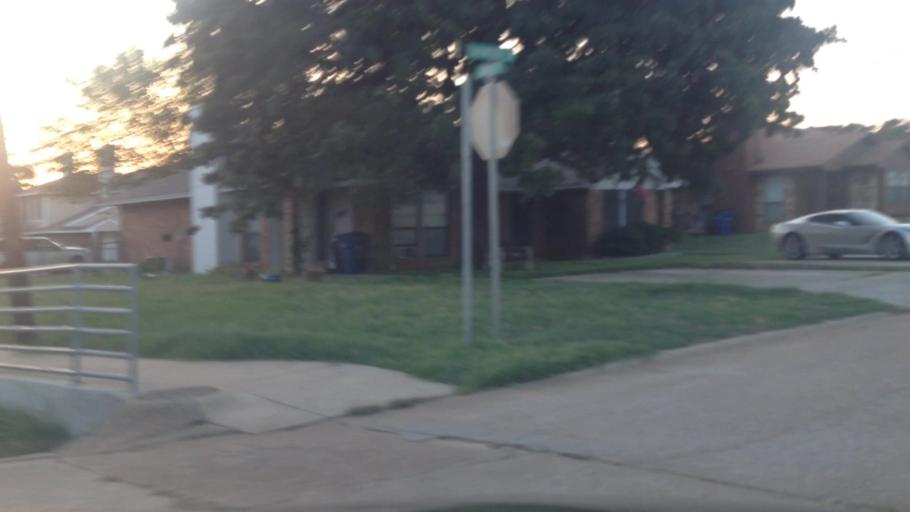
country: US
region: Texas
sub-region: Tarrant County
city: Kennedale
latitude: 32.6490
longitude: -97.2116
